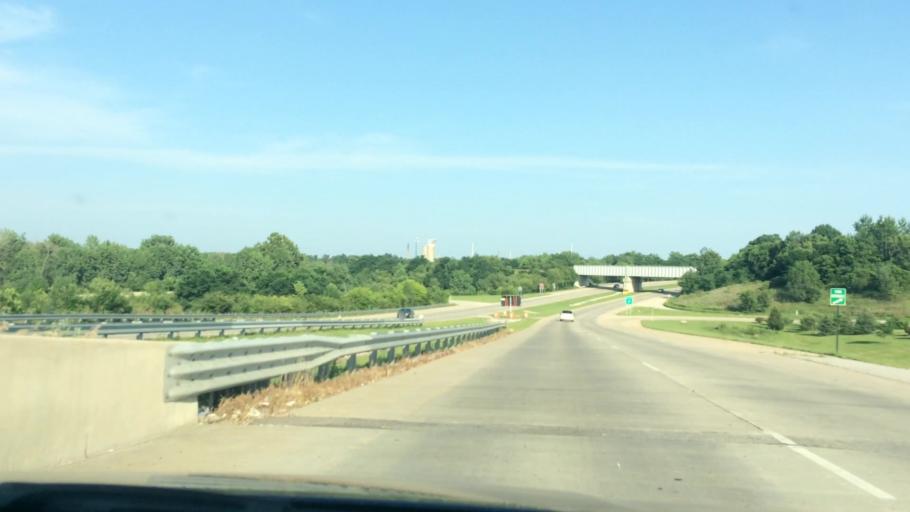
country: US
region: Indiana
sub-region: Tippecanoe County
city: Lafayette
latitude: 40.4483
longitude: -86.8765
